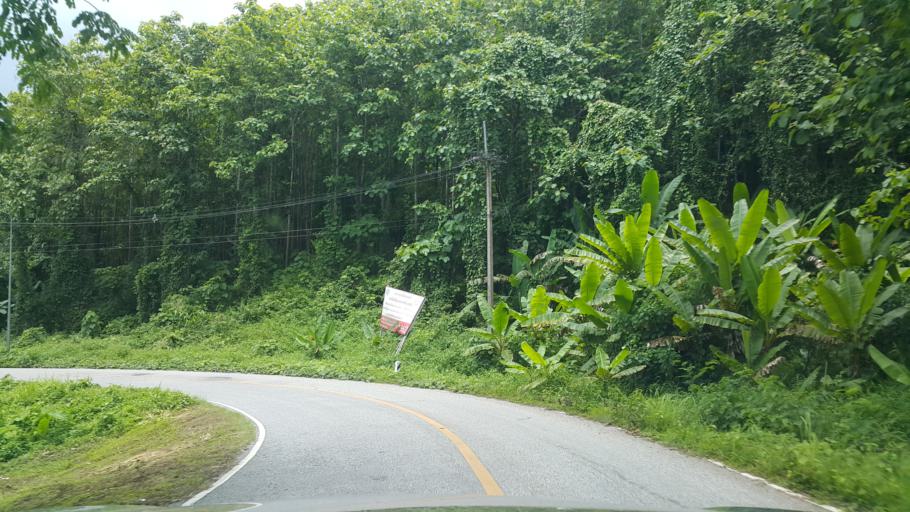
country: TH
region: Loei
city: Na Haeo
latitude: 17.6284
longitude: 100.8945
